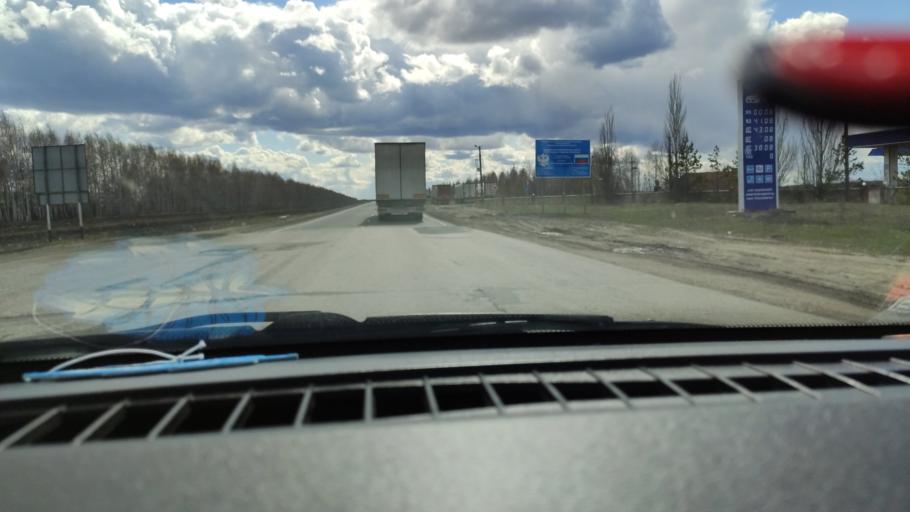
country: RU
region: Samara
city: Syzran'
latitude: 52.9933
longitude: 48.3235
